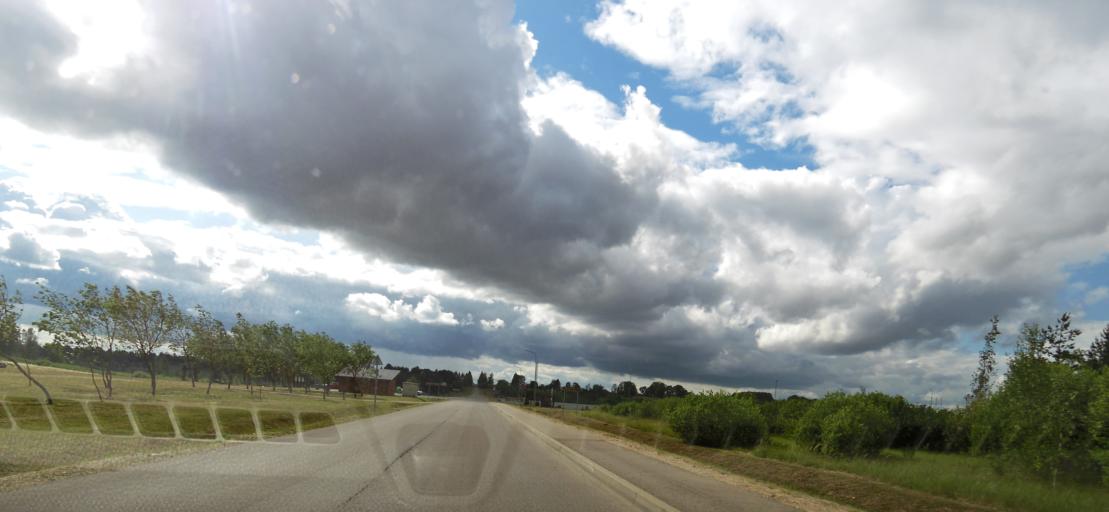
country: LT
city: Kupiskis
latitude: 55.8495
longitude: 24.9782
